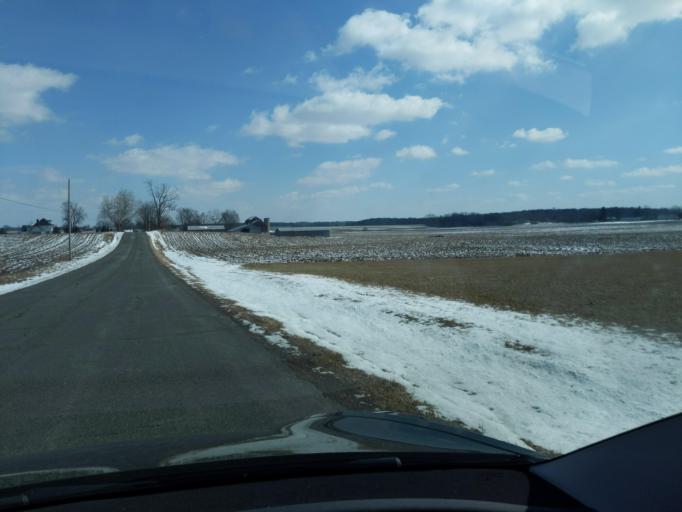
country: US
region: Michigan
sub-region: Ingham County
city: Mason
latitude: 42.6111
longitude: -84.4404
